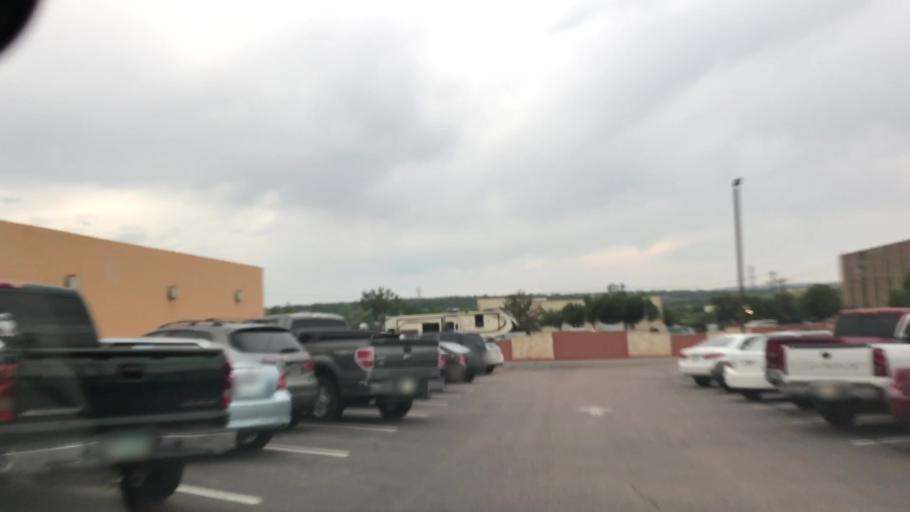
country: US
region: Colorado
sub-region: El Paso County
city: Stratmoor
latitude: 38.7983
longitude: -104.7948
